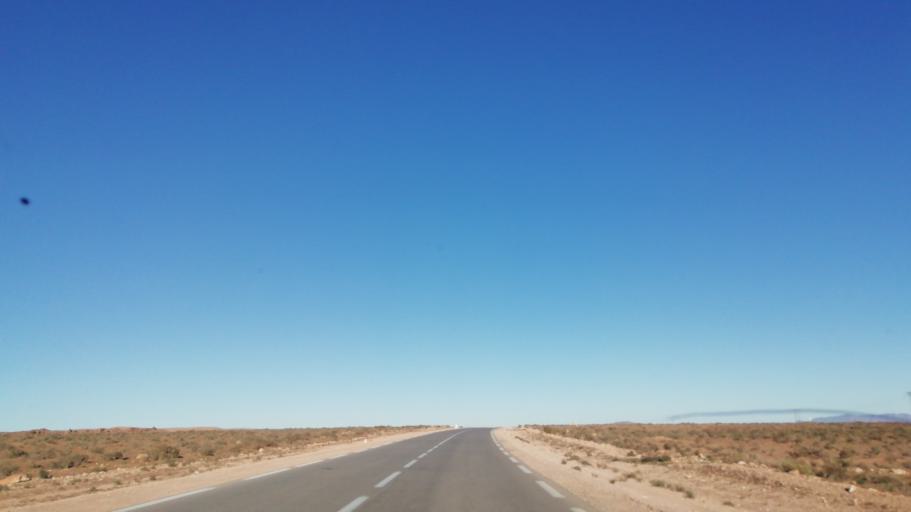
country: DZ
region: El Bayadh
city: El Abiodh Sidi Cheikh
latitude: 33.1320
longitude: 0.2906
